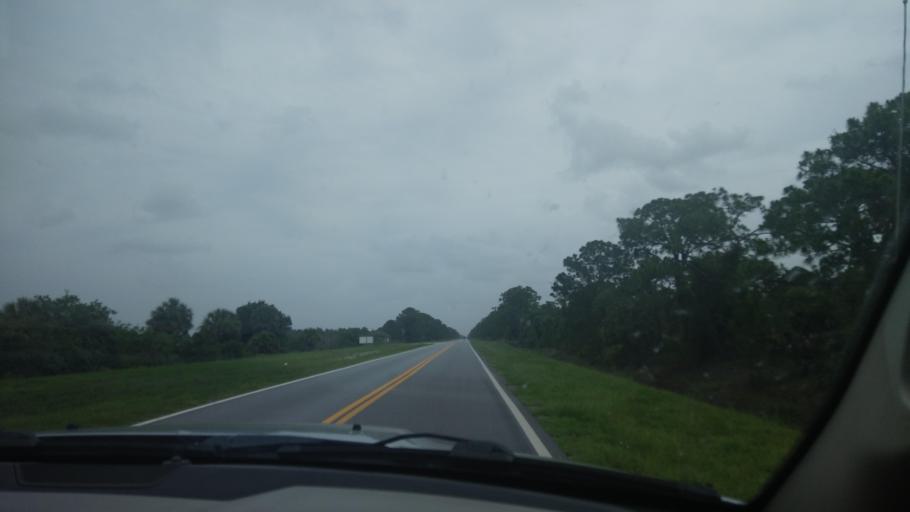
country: US
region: Florida
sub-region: Indian River County
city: Fellsmere
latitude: 27.8431
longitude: -80.6231
